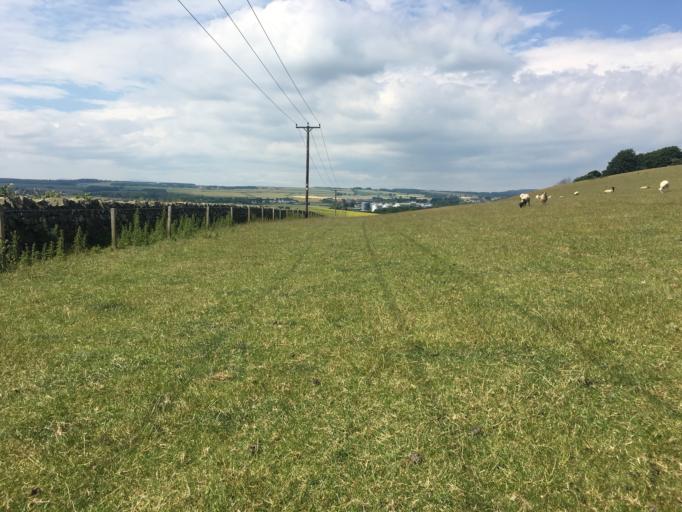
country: GB
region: England
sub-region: Northumberland
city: Belford
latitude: 55.5992
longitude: -1.7894
